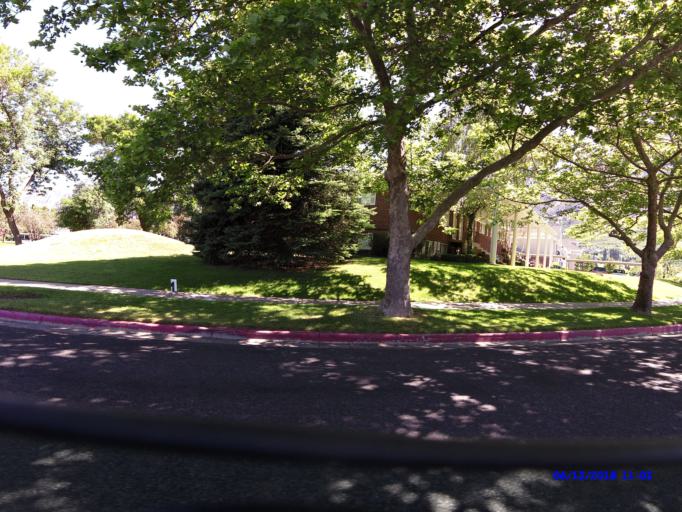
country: US
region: Utah
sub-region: Weber County
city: South Ogden
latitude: 41.2091
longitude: -111.9428
